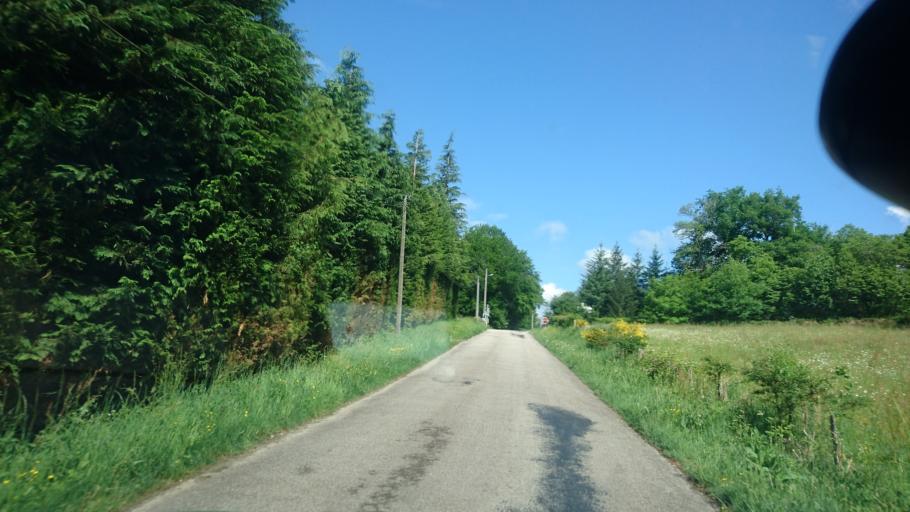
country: FR
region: Limousin
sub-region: Departement de la Haute-Vienne
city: Peyrat-le-Chateau
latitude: 45.8092
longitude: 1.7899
